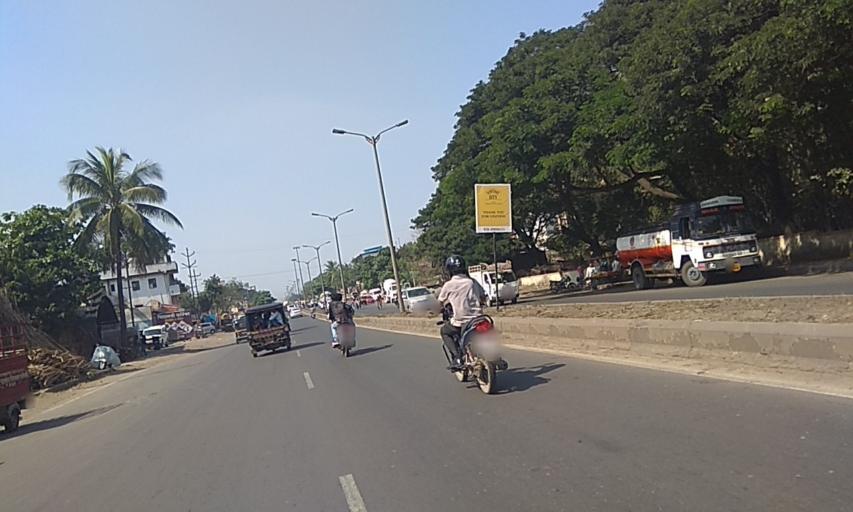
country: IN
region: Maharashtra
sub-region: Pune Division
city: Pune
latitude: 18.4985
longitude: 73.9555
